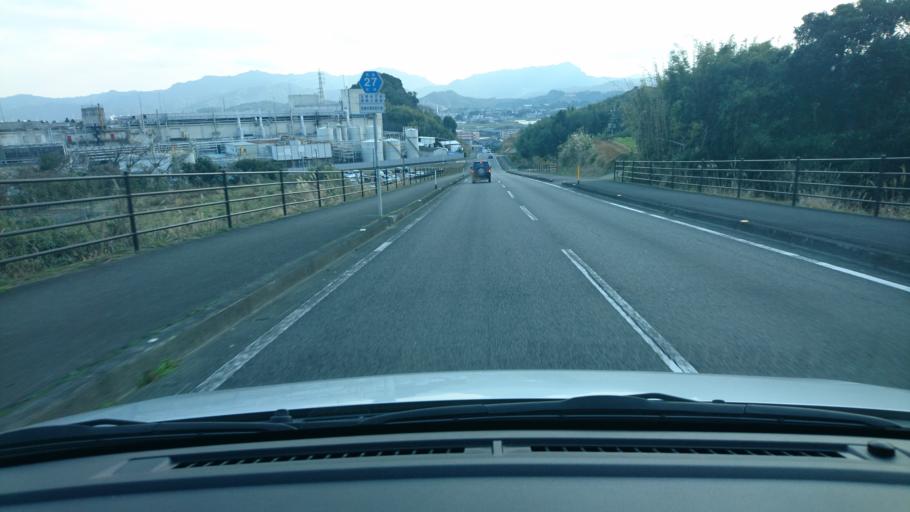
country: JP
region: Miyazaki
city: Miyazaki-shi
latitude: 31.8594
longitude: 131.3995
